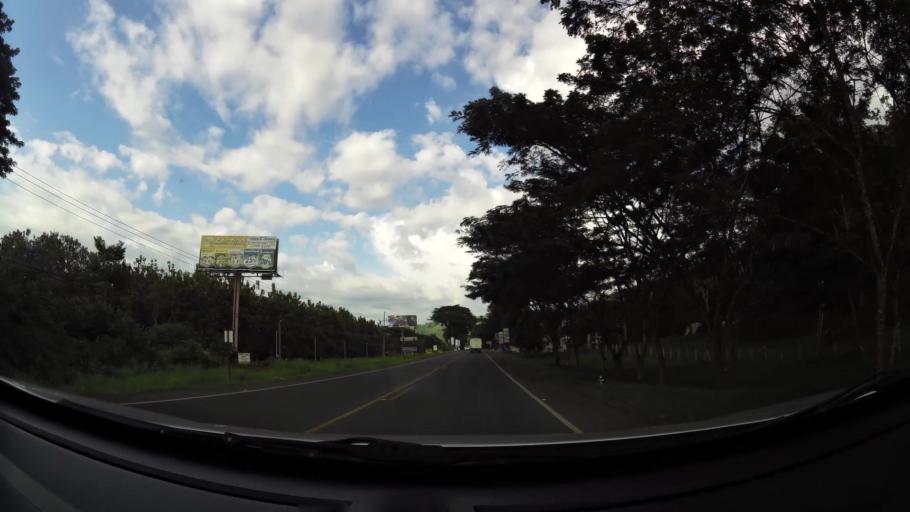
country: CR
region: Puntarenas
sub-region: Canton de Garabito
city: Jaco
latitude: 9.7130
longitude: -84.6352
